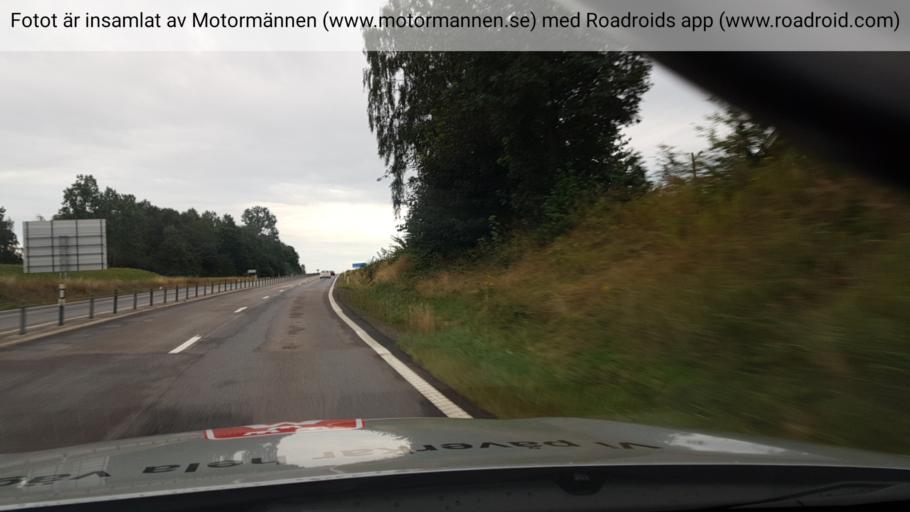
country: SE
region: Halland
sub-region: Laholms Kommun
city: Laholm
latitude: 56.5007
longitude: 13.0401
